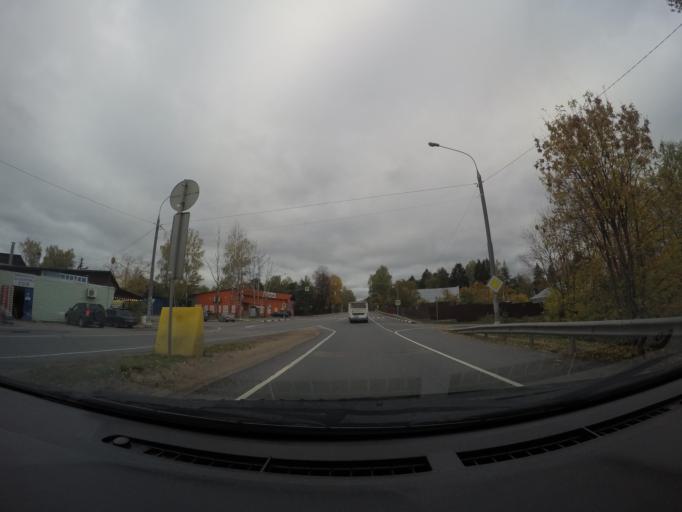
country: RU
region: Moskovskaya
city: Dorokhovo
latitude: 55.6424
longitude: 36.3263
